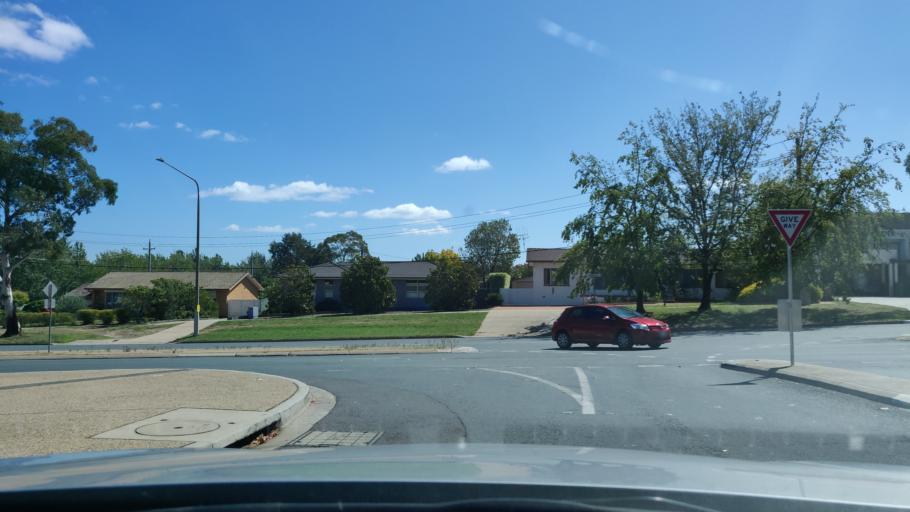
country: AU
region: Australian Capital Territory
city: Macarthur
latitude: -35.3642
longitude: 149.0952
